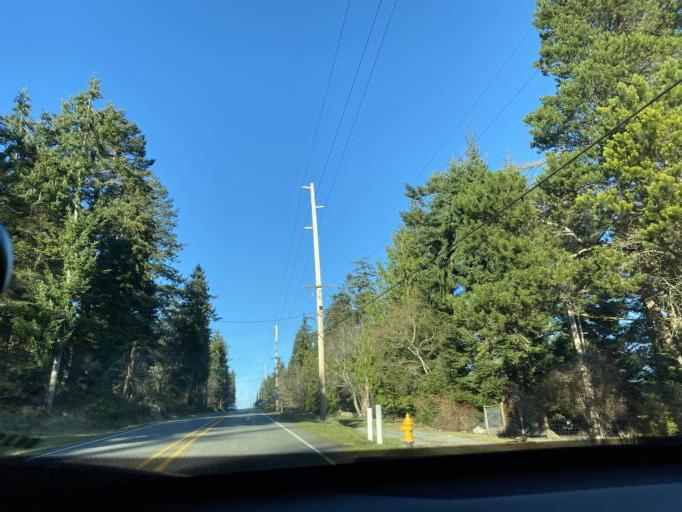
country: US
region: Washington
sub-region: Island County
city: Camano
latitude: 48.1204
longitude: -122.5617
